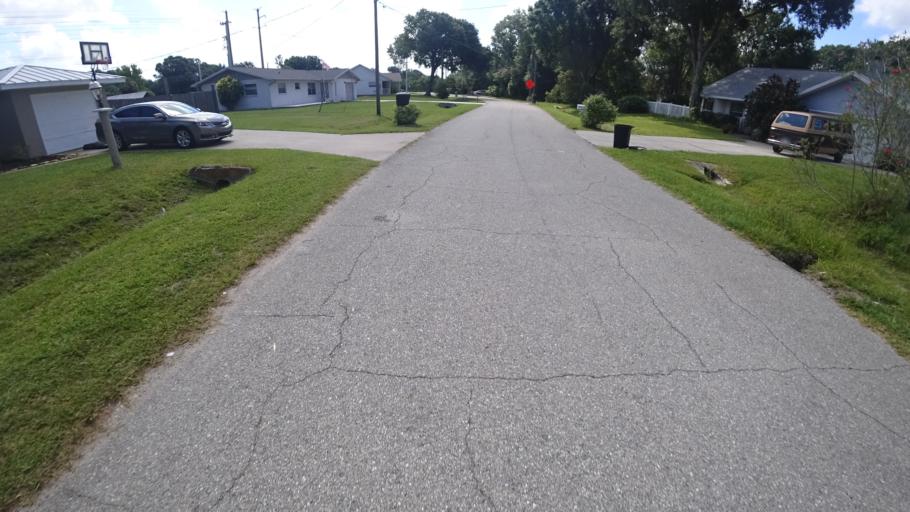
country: US
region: Florida
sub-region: Manatee County
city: Samoset
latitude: 27.4833
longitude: -82.4908
